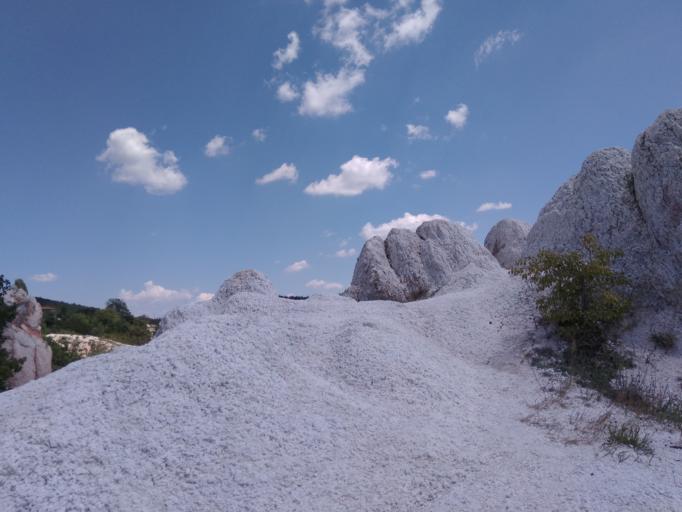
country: BG
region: Kurdzhali
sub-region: Obshtina Kurdzhali
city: Kurdzhali
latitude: 41.6565
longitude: 25.3992
